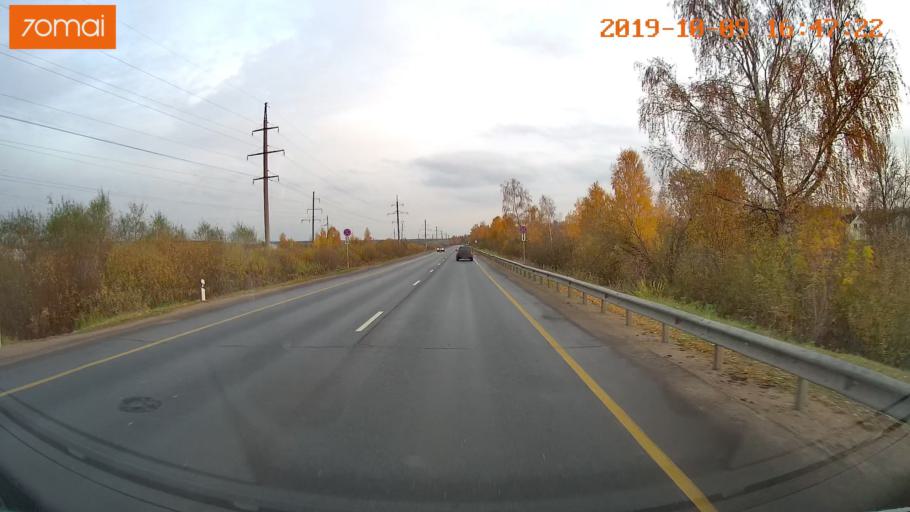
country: RU
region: Kostroma
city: Volgorechensk
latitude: 57.4373
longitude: 41.1770
